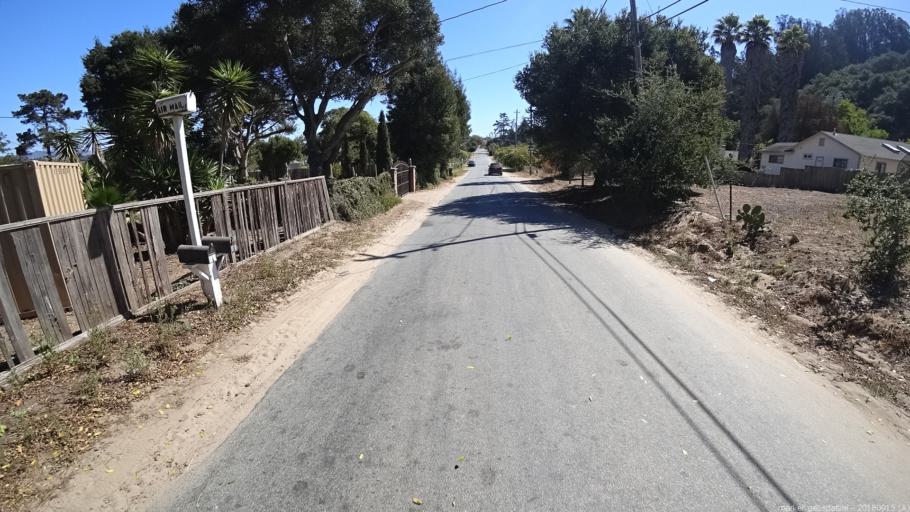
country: US
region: California
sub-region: Monterey County
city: Las Lomas
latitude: 36.8538
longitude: -121.7082
